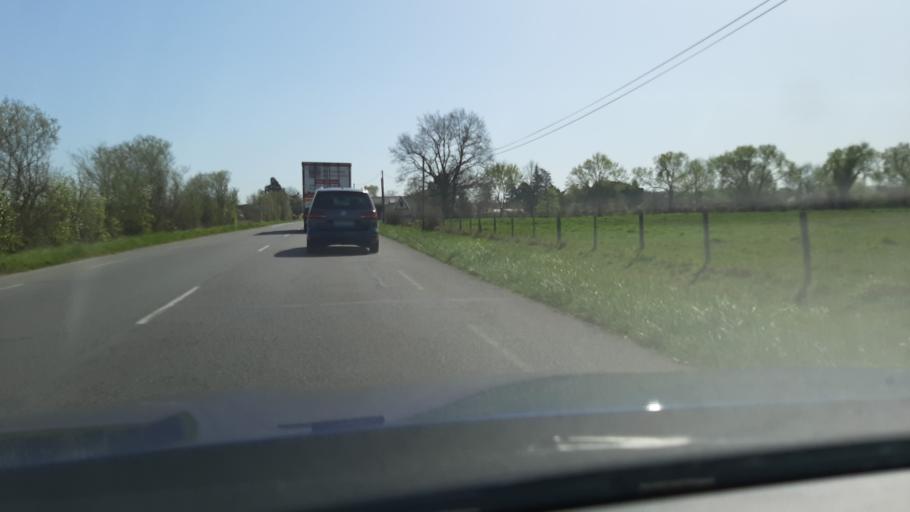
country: FR
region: Pays de la Loire
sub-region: Departement de Maine-et-Loire
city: Ecouflant
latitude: 47.5189
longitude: -0.4854
